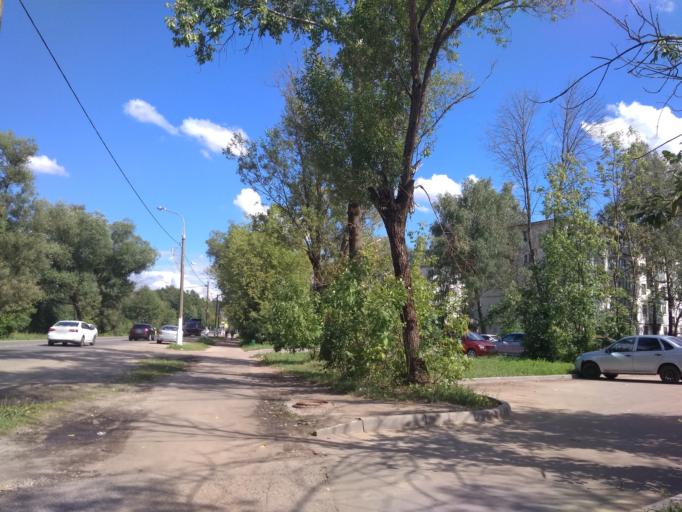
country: RU
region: Moskovskaya
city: Orekhovo-Zuyevo
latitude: 55.8022
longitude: 39.0019
